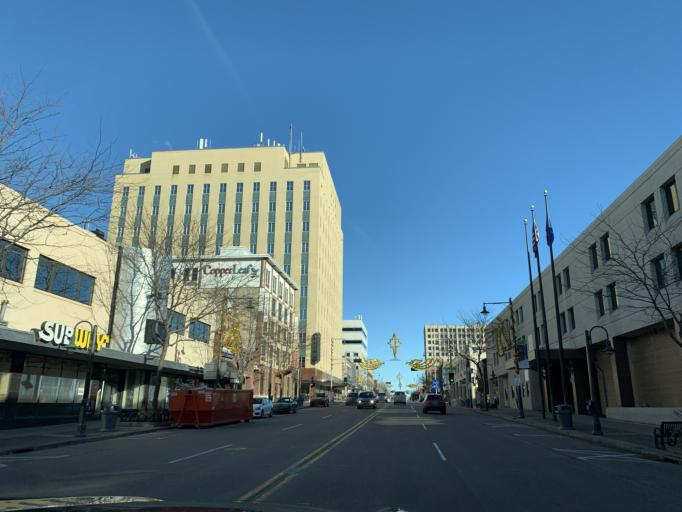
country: US
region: Wisconsin
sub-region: Outagamie County
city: Appleton
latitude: 44.2618
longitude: -88.4098
